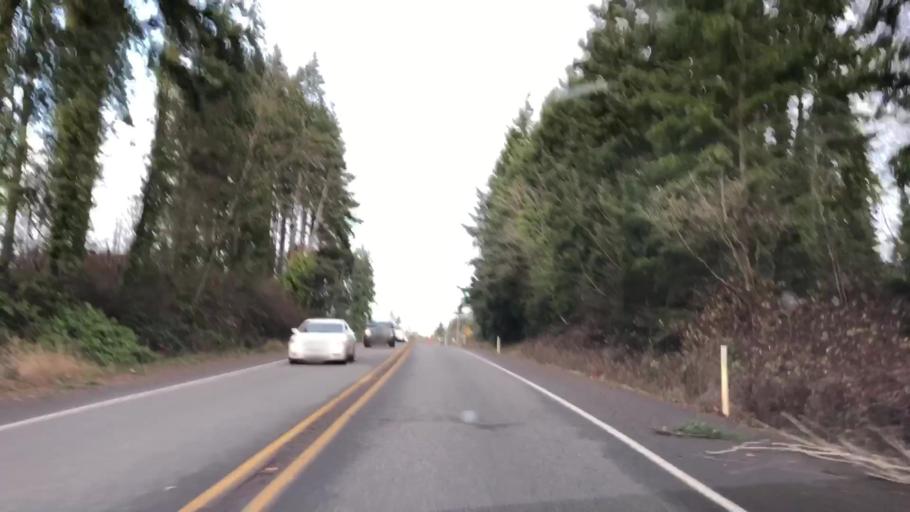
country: US
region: Washington
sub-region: Kitsap County
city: Bainbridge Island
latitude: 47.6426
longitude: -122.5175
